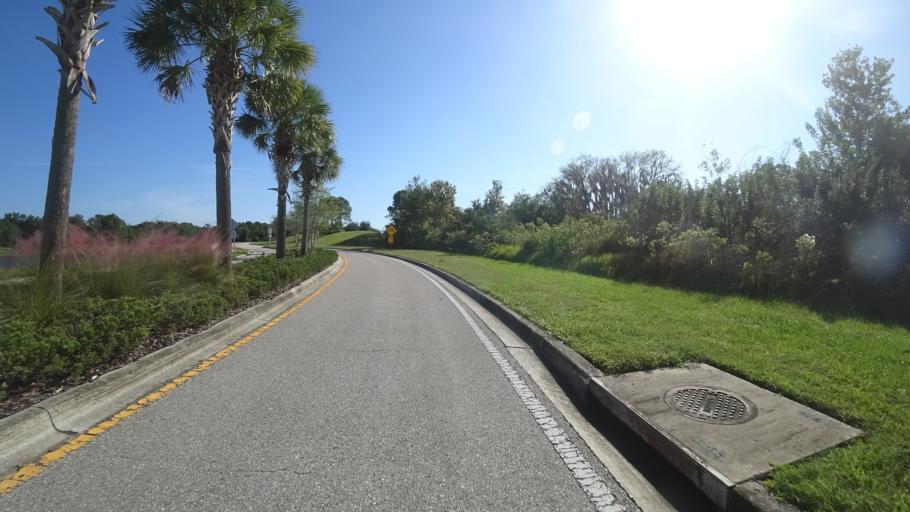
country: US
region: Florida
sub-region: Sarasota County
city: The Meadows
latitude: 27.4199
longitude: -82.4193
